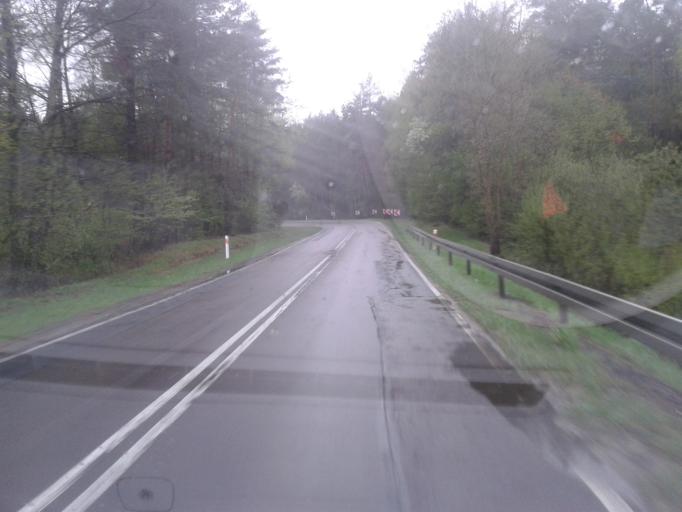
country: PL
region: Subcarpathian Voivodeship
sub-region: Powiat lubaczowski
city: Narol
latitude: 50.3725
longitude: 23.3716
